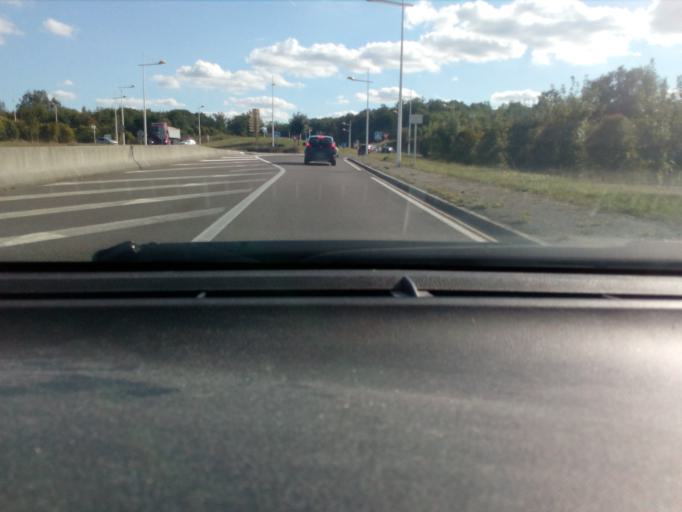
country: FR
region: Poitou-Charentes
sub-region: Departement de la Charente
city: Soyaux
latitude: 45.6519
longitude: 0.2089
